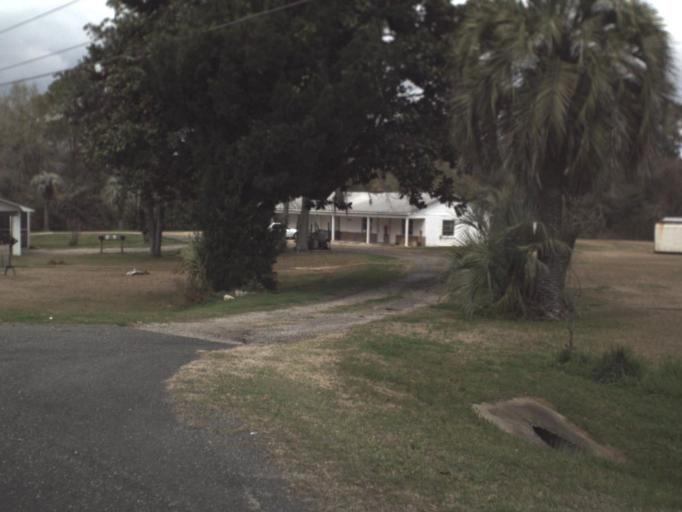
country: US
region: Florida
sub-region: Leon County
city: Tallahassee
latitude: 30.4272
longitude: -84.1868
